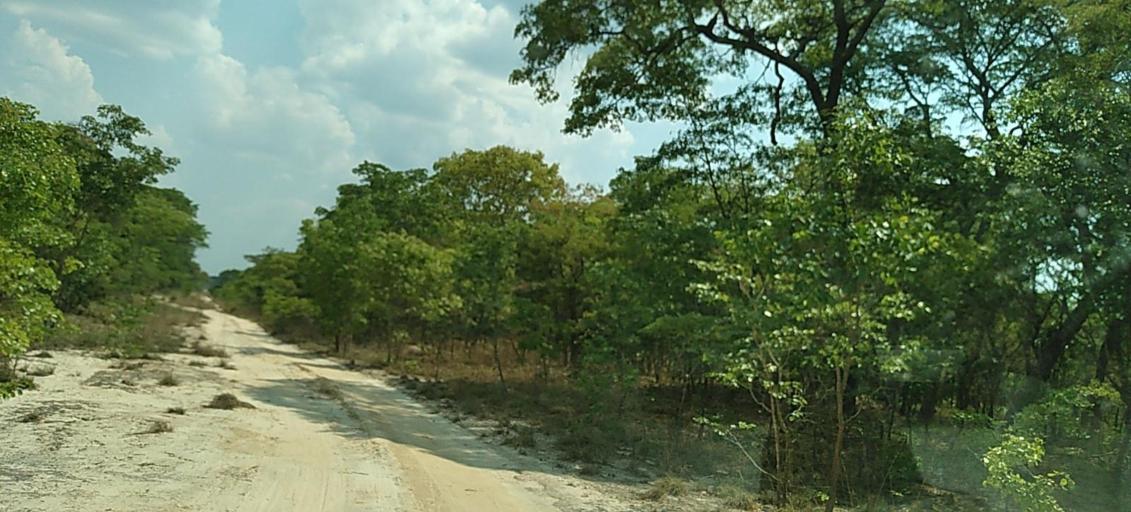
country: ZM
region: Copperbelt
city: Mpongwe
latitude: -13.8279
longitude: 27.9410
